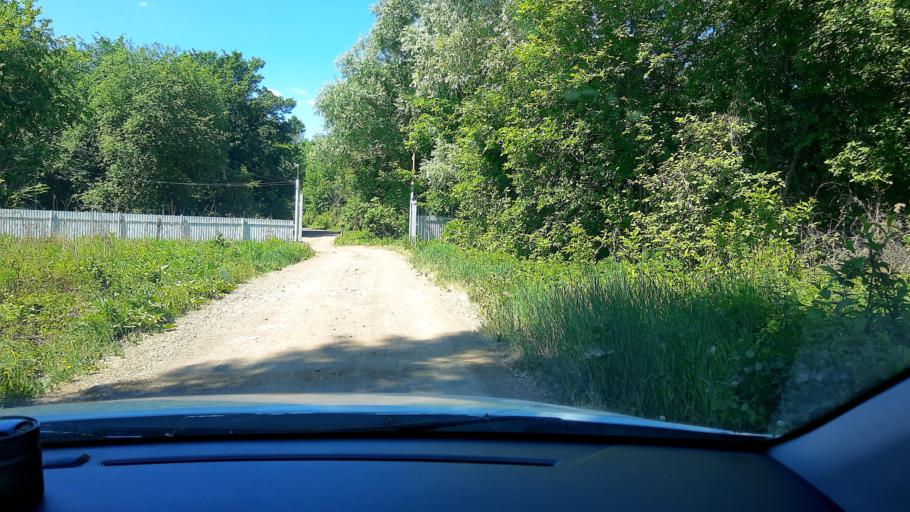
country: RU
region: Bashkortostan
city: Mikhaylovka
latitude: 54.7385
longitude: 55.8628
